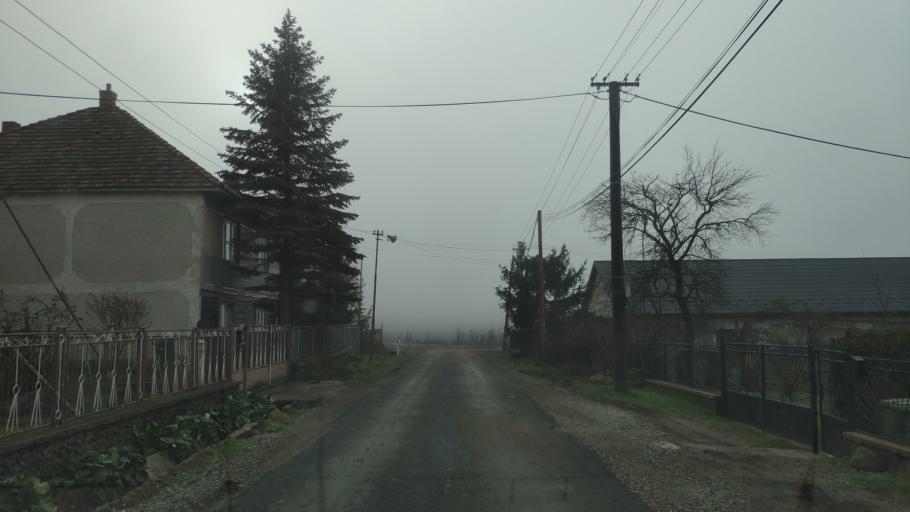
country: SK
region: Kosicky
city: Kosice
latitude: 48.7059
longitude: 21.4424
